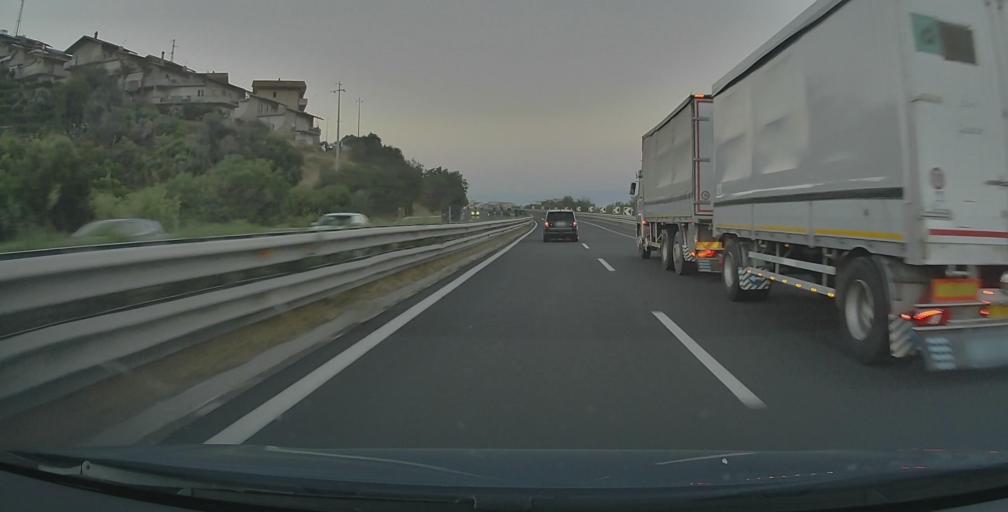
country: IT
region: Sicily
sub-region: Messina
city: Nizza di Sicilia
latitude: 37.9910
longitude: 15.4080
